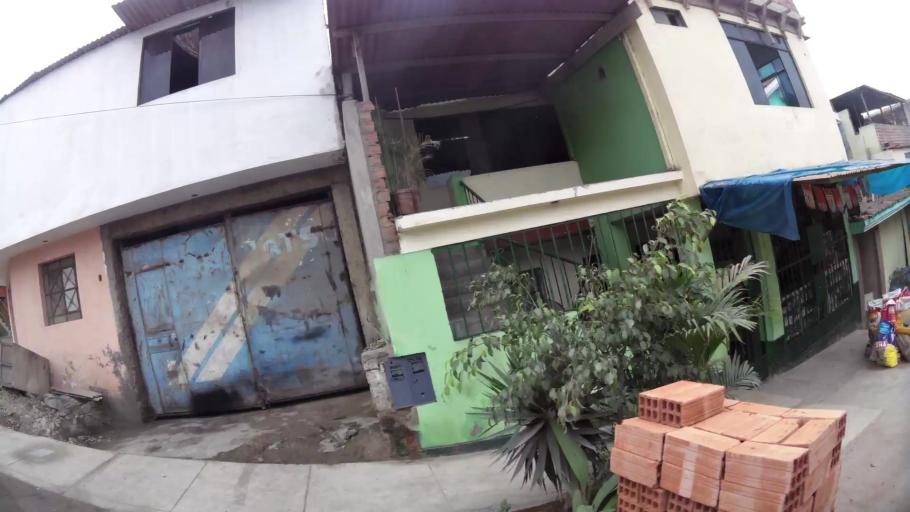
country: PE
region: Lima
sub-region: Lima
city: Surco
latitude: -12.1794
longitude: -76.9509
